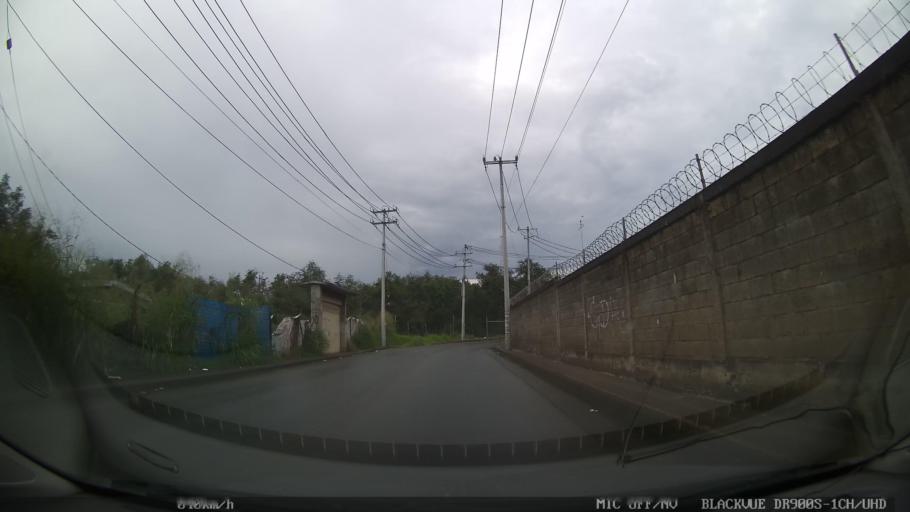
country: MX
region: Michoacan
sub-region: Uruapan
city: Santa Rosa (Santa Barbara)
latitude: 19.3846
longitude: -102.0493
